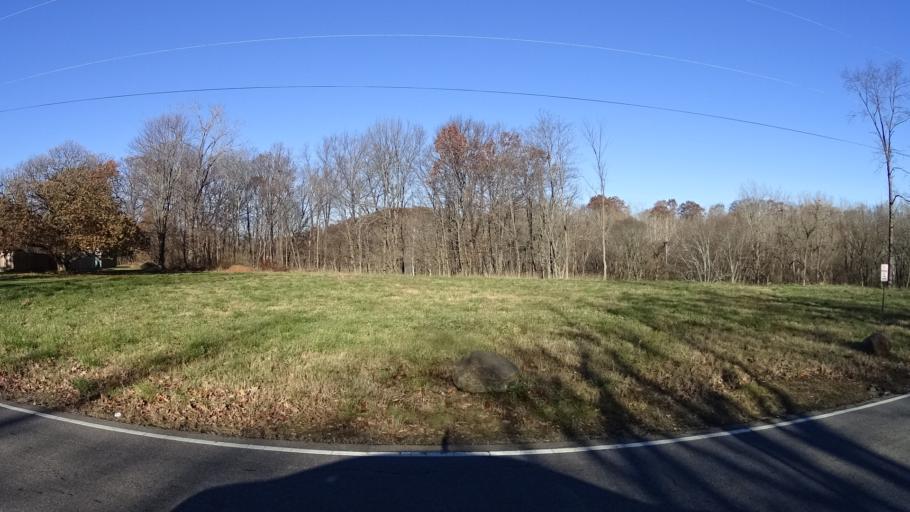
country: US
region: Ohio
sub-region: Lorain County
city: Sheffield
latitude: 41.4099
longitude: -82.0930
